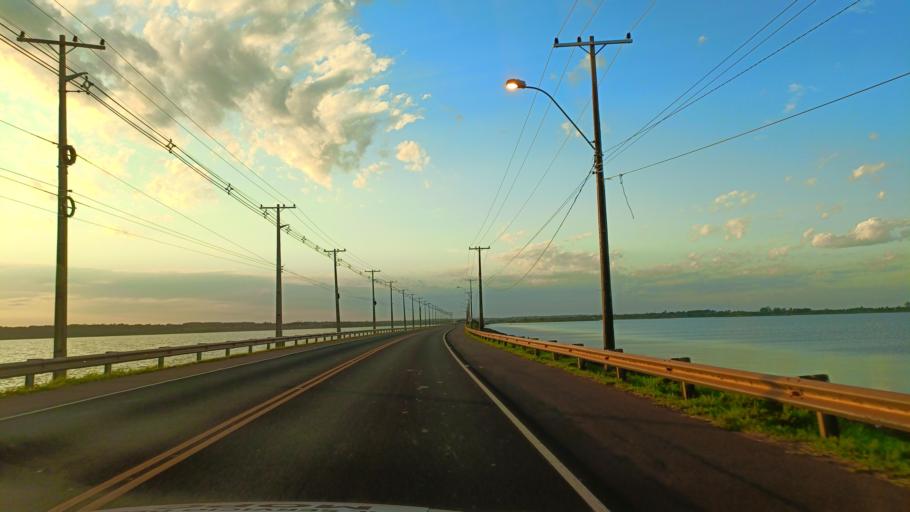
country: PY
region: Itapua
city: Carmen del Parana
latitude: -27.2022
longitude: -56.1781
